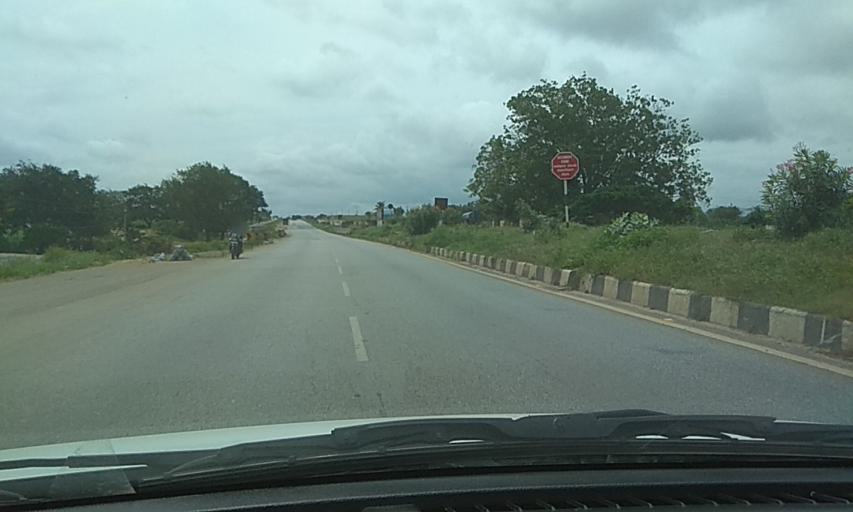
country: IN
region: Karnataka
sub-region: Davanagere
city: Mayakonda
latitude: 14.3399
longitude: 76.2092
